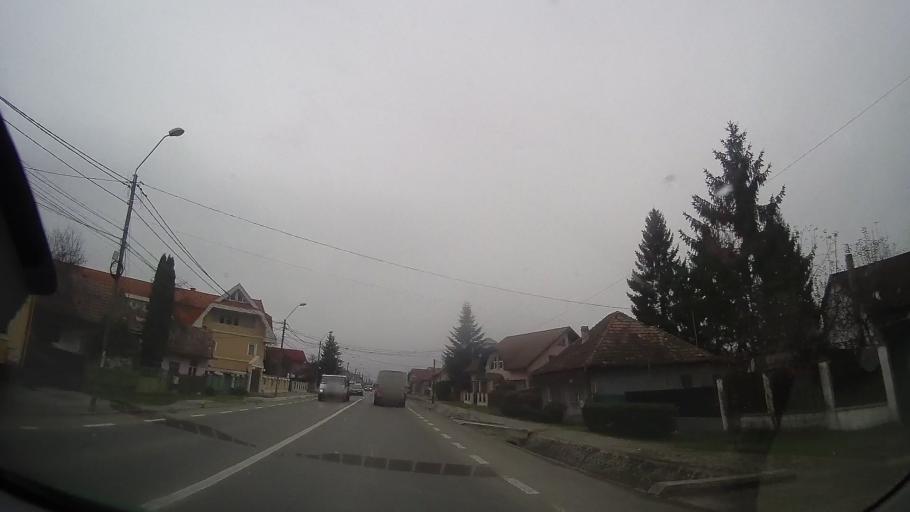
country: RO
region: Mures
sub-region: Comuna Santana de Mures
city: Santana de Mures
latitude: 46.5861
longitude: 24.5394
